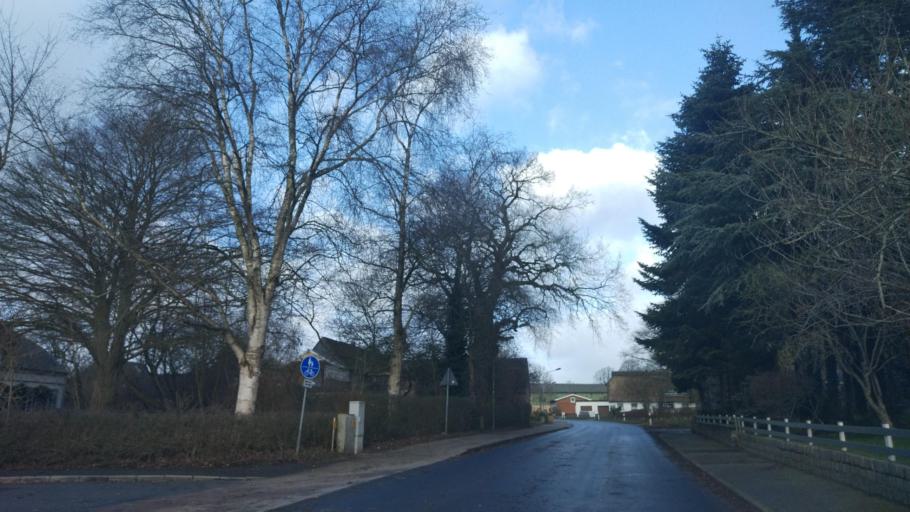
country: DE
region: Schleswig-Holstein
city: Taarstedt
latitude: 54.5640
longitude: 9.6783
